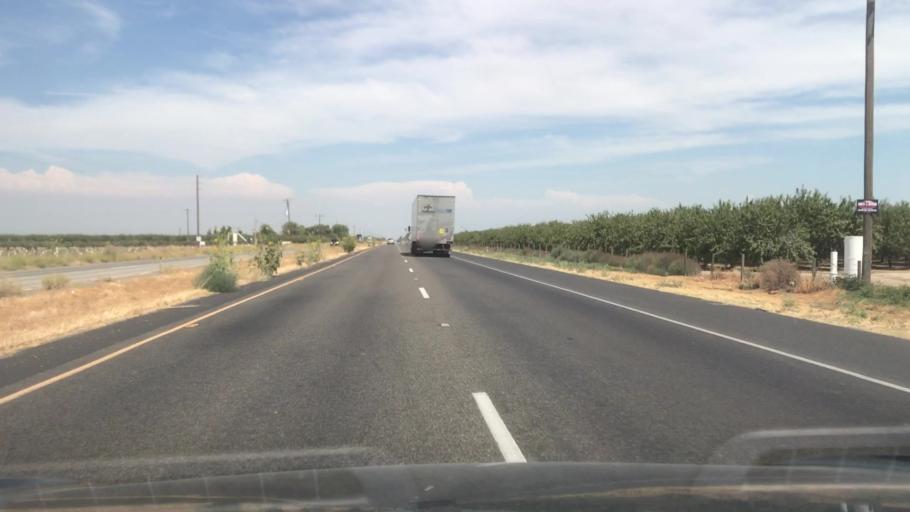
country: US
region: California
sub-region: Merced County
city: Dos Palos
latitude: 37.0835
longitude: -120.4626
